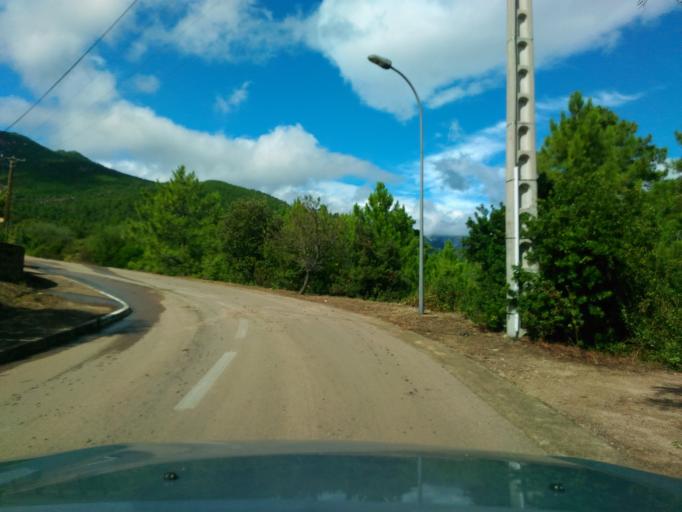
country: FR
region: Corsica
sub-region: Departement de la Corse-du-Sud
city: Porto-Vecchio
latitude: 41.7110
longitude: 9.3096
